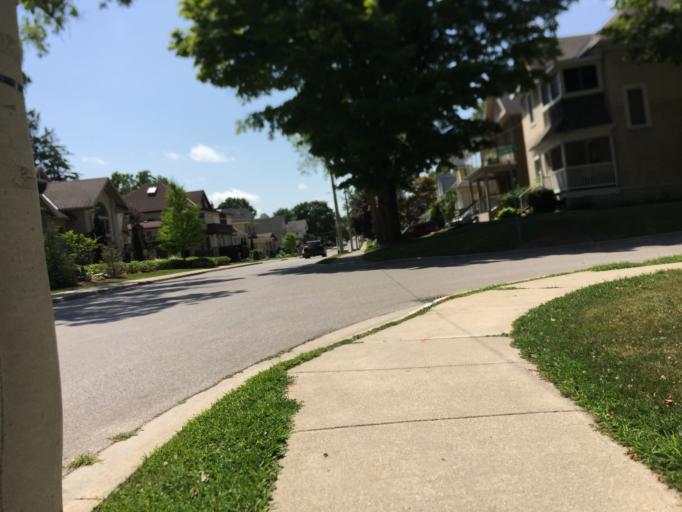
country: CA
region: Ontario
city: Stratford
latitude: 43.3762
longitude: -80.9763
